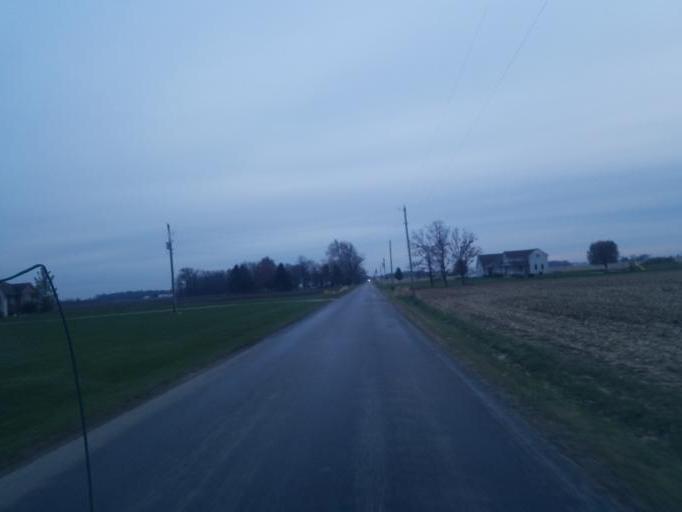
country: US
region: Indiana
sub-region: Adams County
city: Decatur
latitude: 40.7845
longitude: -85.0148
